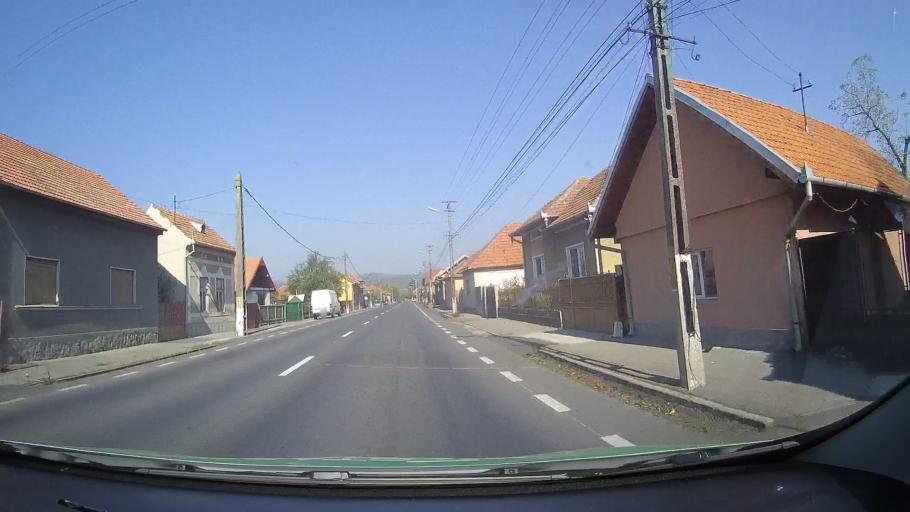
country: RO
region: Hunedoara
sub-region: Comuna Ilia
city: Ilia
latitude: 45.9361
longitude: 22.6513
